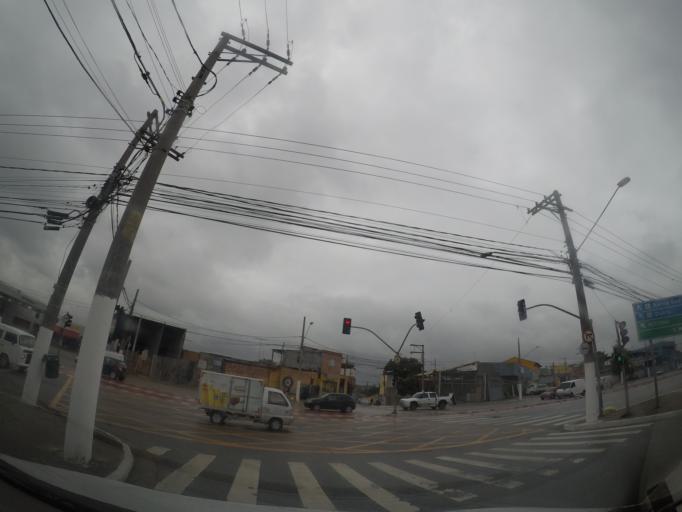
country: BR
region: Sao Paulo
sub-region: Guarulhos
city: Guarulhos
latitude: -23.4841
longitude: -46.4690
